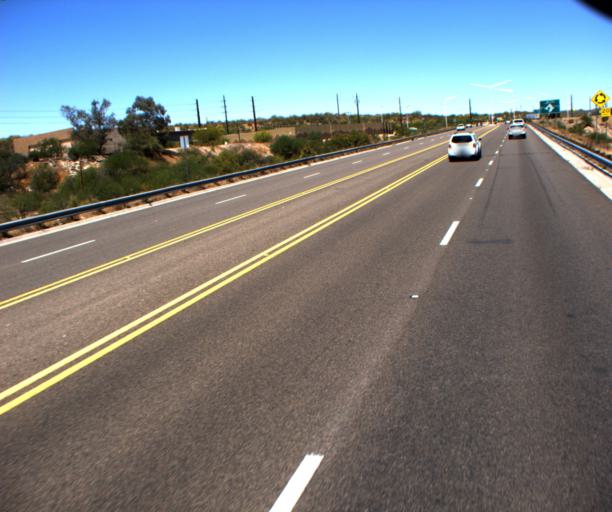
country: US
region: Arizona
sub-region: Maricopa County
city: Wickenburg
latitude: 33.9832
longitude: -112.7370
